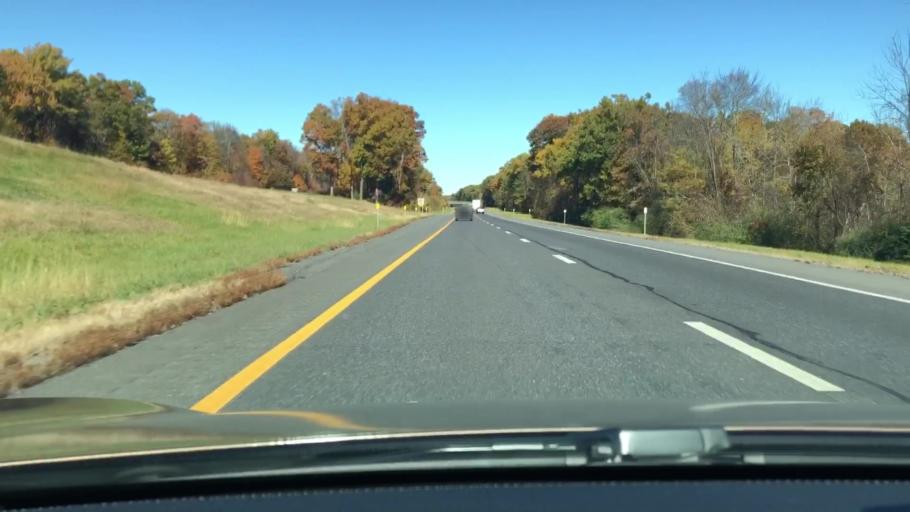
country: US
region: New York
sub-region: Ulster County
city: New Paltz
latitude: 41.7644
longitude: -74.0547
